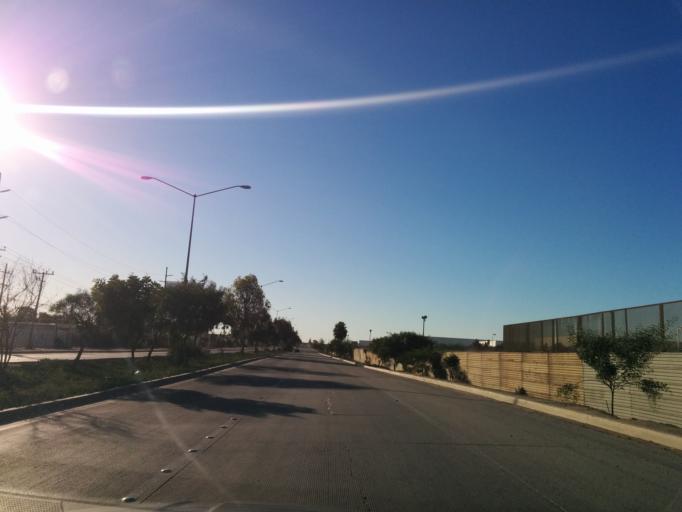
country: MX
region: Baja California
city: Tijuana
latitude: 32.5490
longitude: -116.9514
